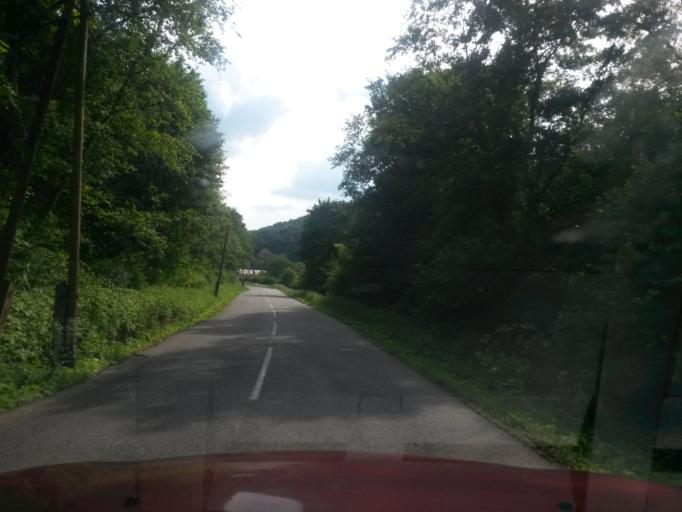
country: SK
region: Presovsky
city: Snina
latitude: 49.1199
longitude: 22.0759
